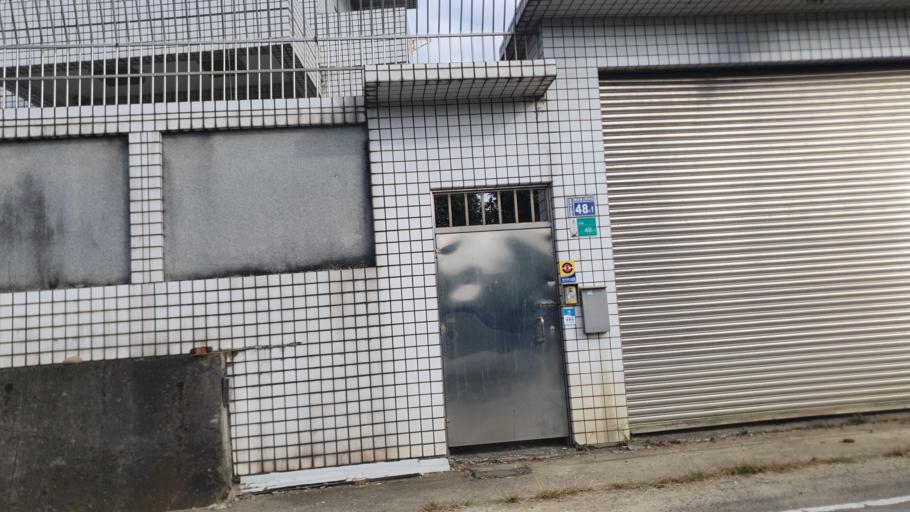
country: TW
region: Taiwan
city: Yujing
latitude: 23.0121
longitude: 120.4170
